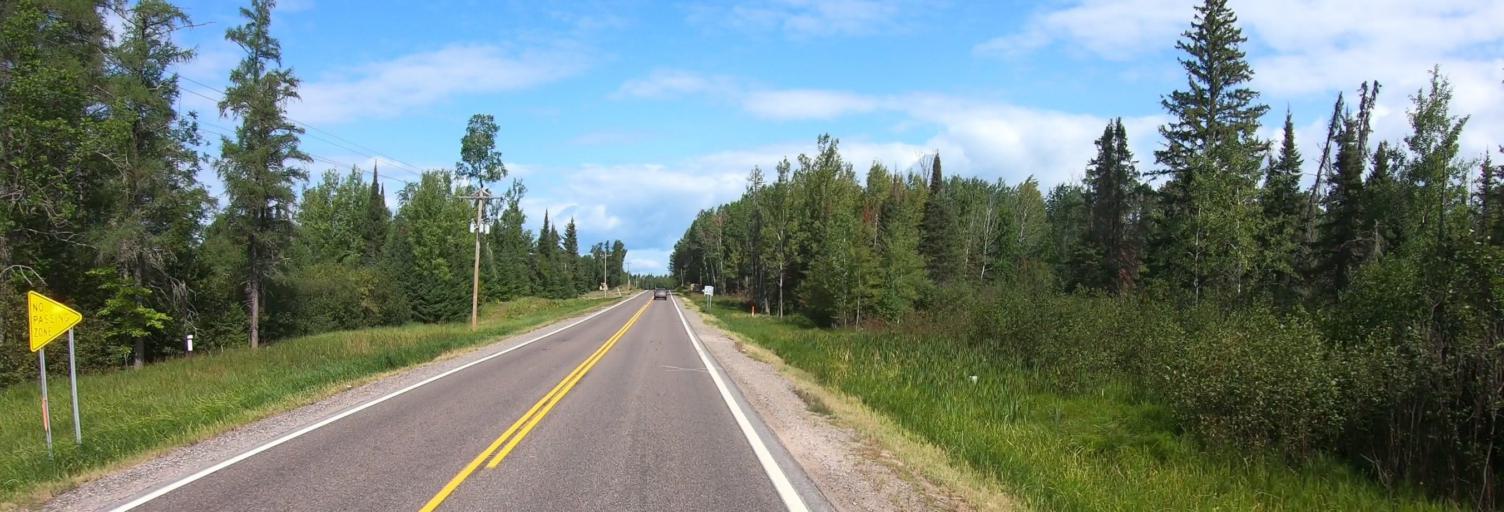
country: US
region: Minnesota
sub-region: Saint Louis County
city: Mountain Iron
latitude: 47.9214
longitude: -92.6586
